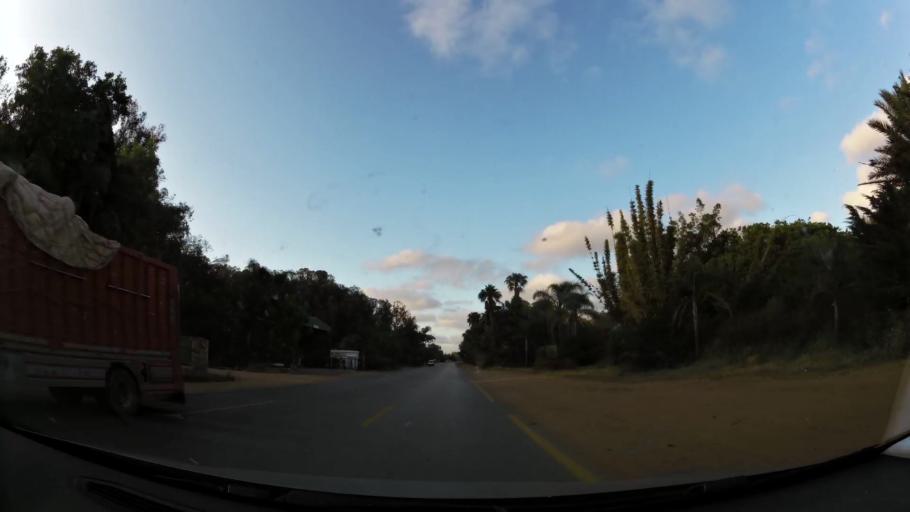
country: MA
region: Gharb-Chrarda-Beni Hssen
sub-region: Kenitra Province
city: Kenitra
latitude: 34.2151
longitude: -6.6672
